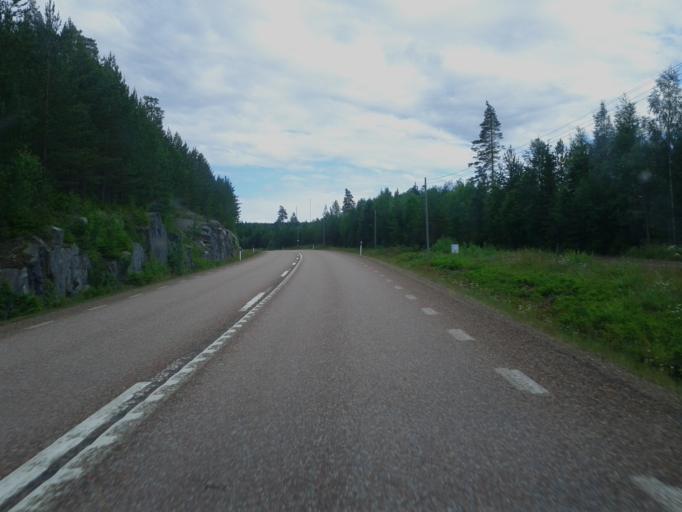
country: SE
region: Dalarna
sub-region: Faluns Kommun
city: Bjursas
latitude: 60.7895
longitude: 15.2811
